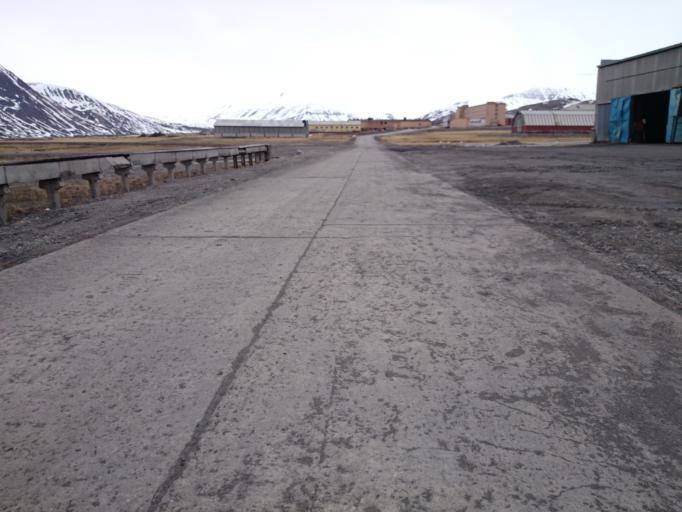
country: SJ
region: Svalbard
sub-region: Spitsbergen
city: Longyearbyen
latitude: 78.6536
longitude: 16.3396
